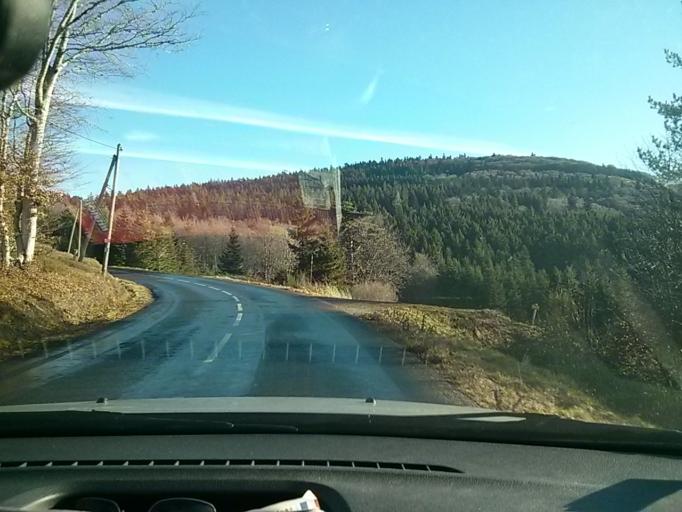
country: FR
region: Rhone-Alpes
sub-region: Departement de la Loire
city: Bourg-Argental
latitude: 45.3681
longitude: 4.5407
